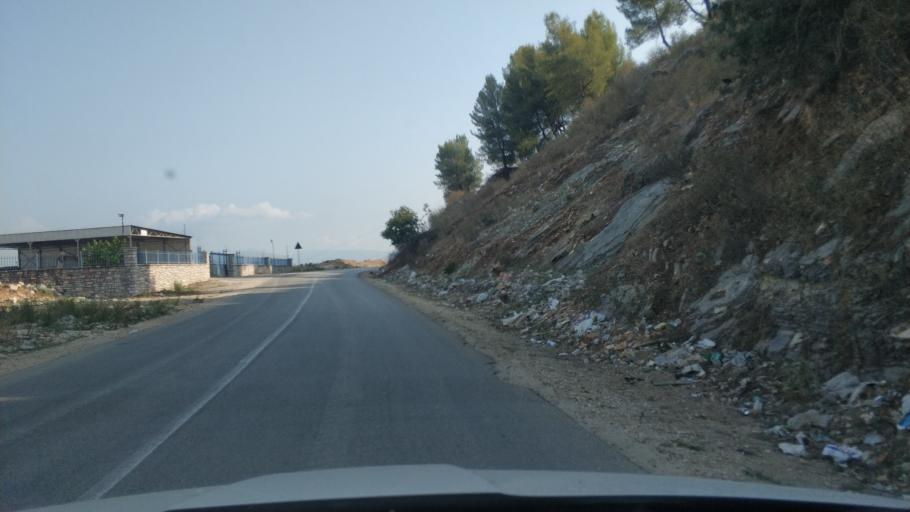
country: AL
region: Vlore
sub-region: Rrethi i Sarandes
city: Sarande
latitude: 39.8698
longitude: 20.0304
